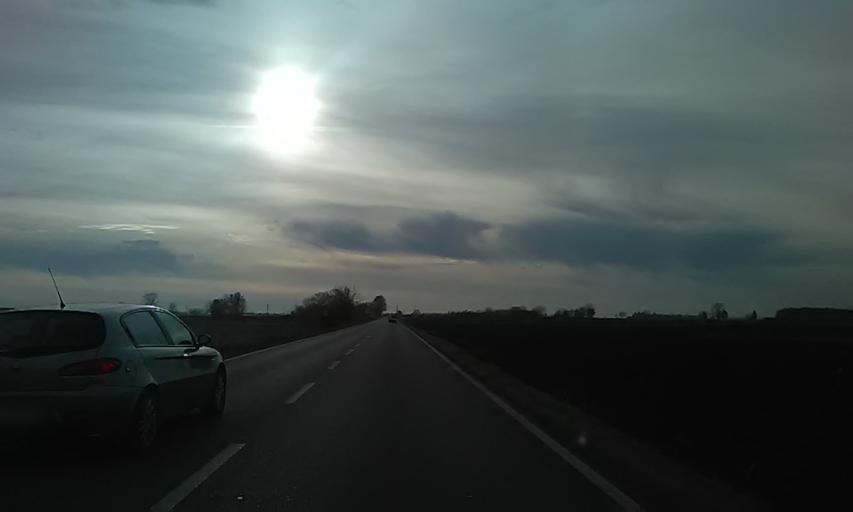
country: IT
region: Piedmont
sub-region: Provincia di Torino
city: Villareggia
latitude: 45.2897
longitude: 7.9970
